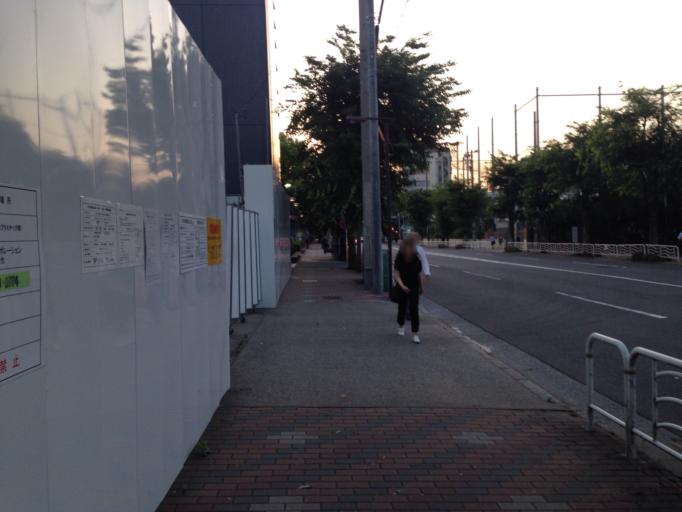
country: JP
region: Tokyo
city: Urayasu
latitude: 35.6652
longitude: 139.7959
